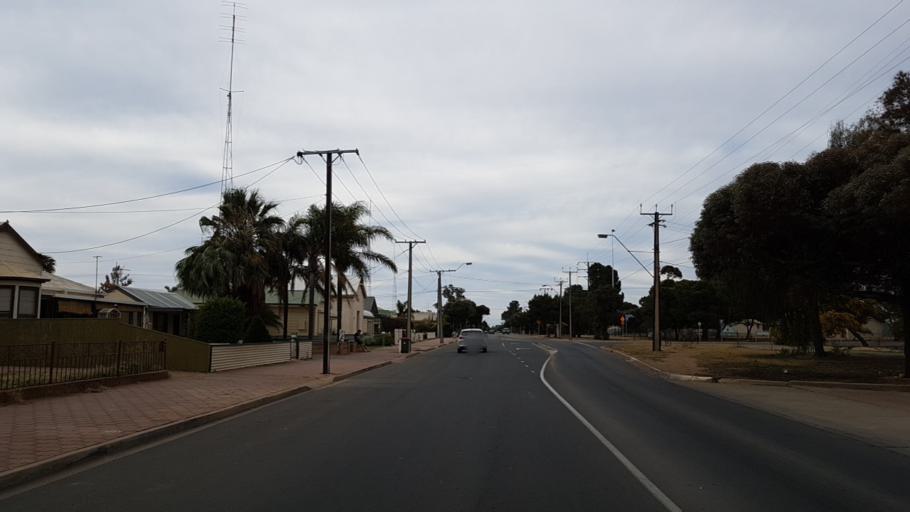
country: AU
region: South Australia
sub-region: Port Pirie City and Dists
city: Port Pirie
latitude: -33.1845
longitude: 138.0039
